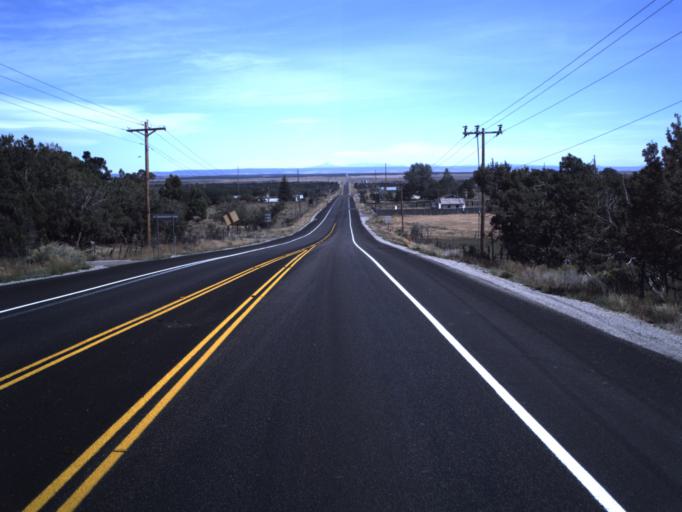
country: US
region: Utah
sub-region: San Juan County
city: Monticello
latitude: 37.8728
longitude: -109.3230
